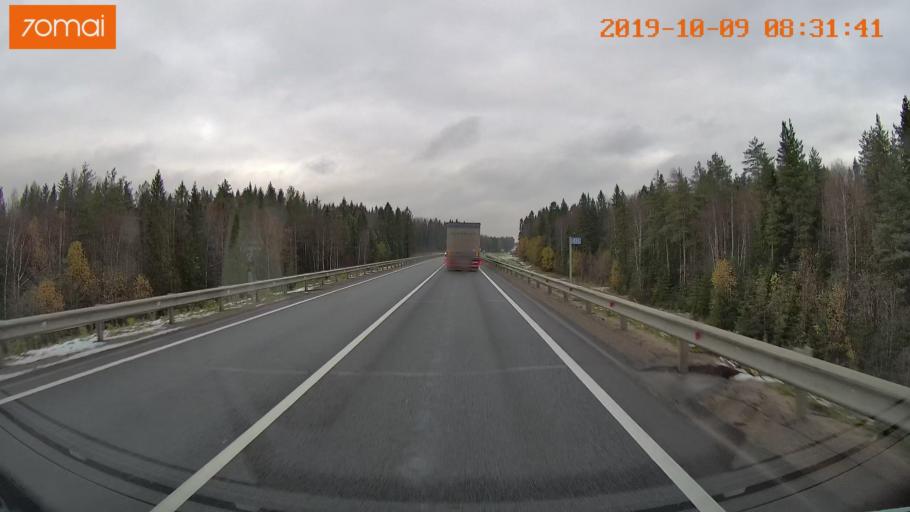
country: RU
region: Vologda
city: Gryazovets
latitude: 58.8571
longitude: 40.2004
